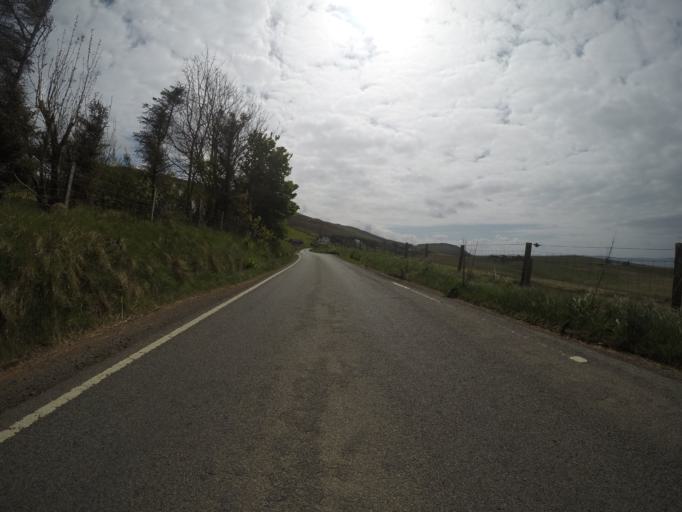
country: GB
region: Scotland
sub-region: Highland
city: Portree
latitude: 57.6152
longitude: -6.3712
